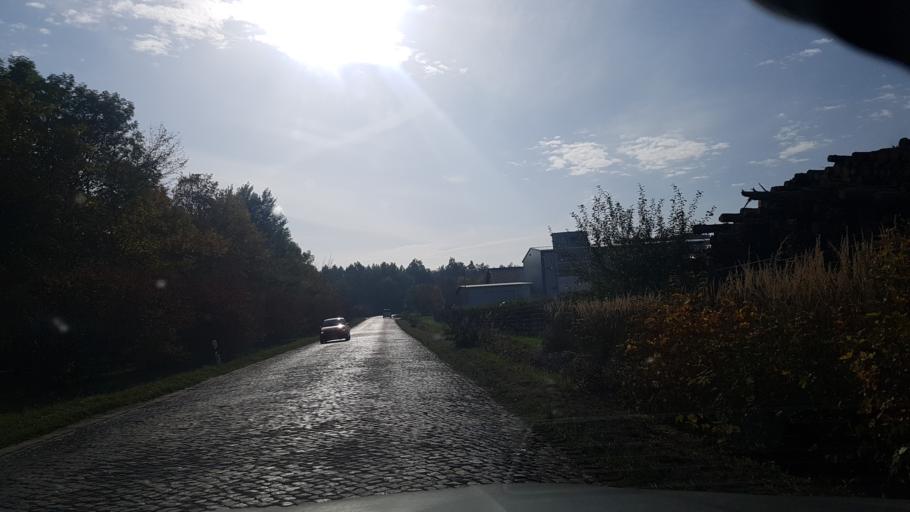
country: DE
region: Saxony
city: Struppen
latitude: 50.9125
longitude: 14.0274
